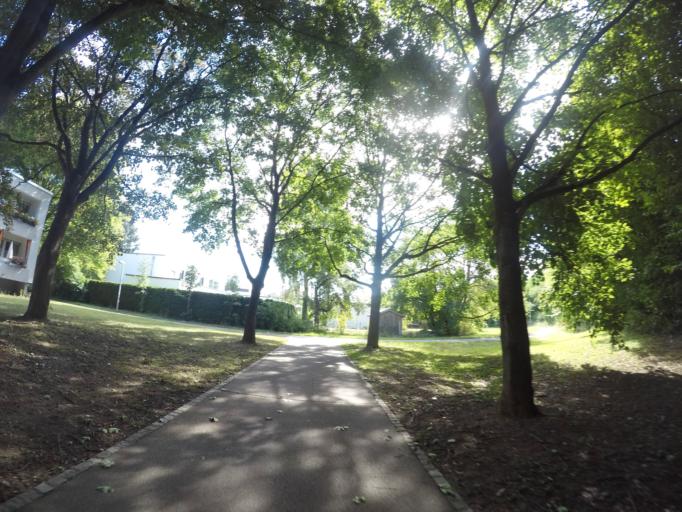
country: DE
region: Baden-Wuerttemberg
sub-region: Tuebingen Region
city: Ulm
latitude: 48.3571
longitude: 9.9711
